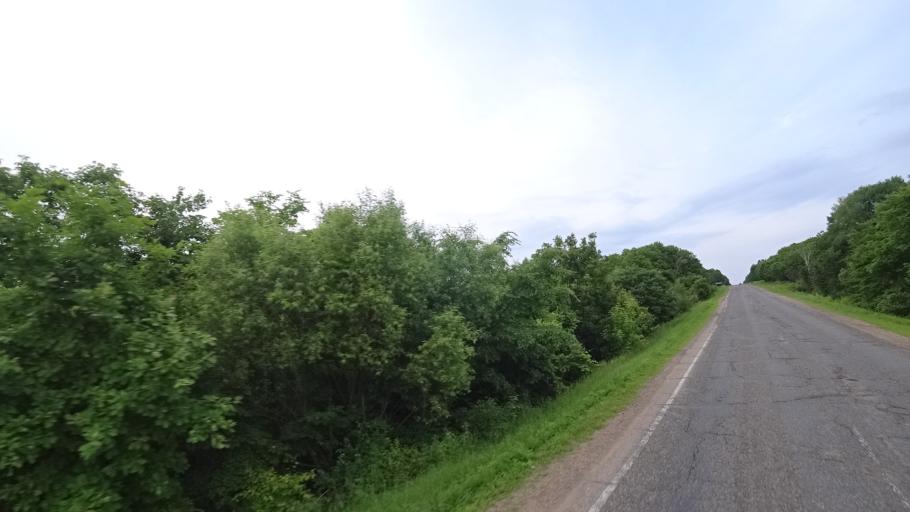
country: RU
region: Primorskiy
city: Novosysoyevka
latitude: 44.2343
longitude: 133.3815
